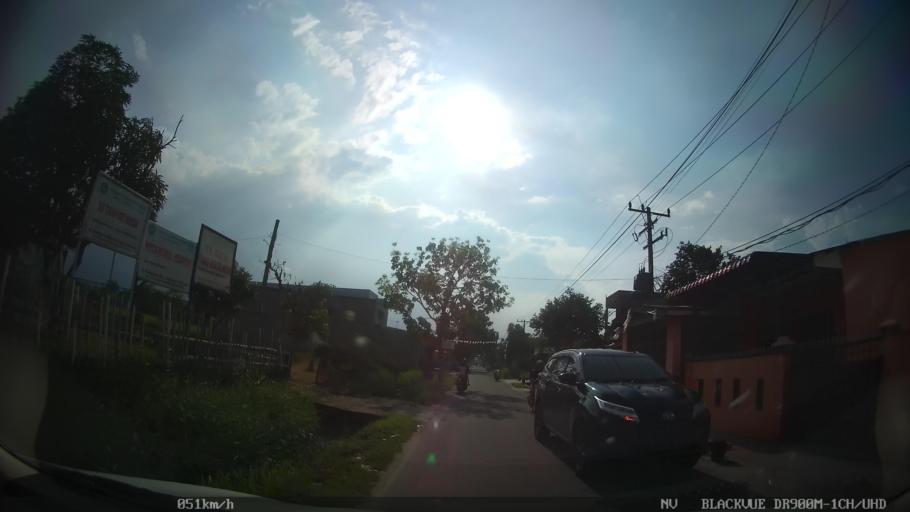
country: ID
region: North Sumatra
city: Percut
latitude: 3.5938
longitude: 98.7766
